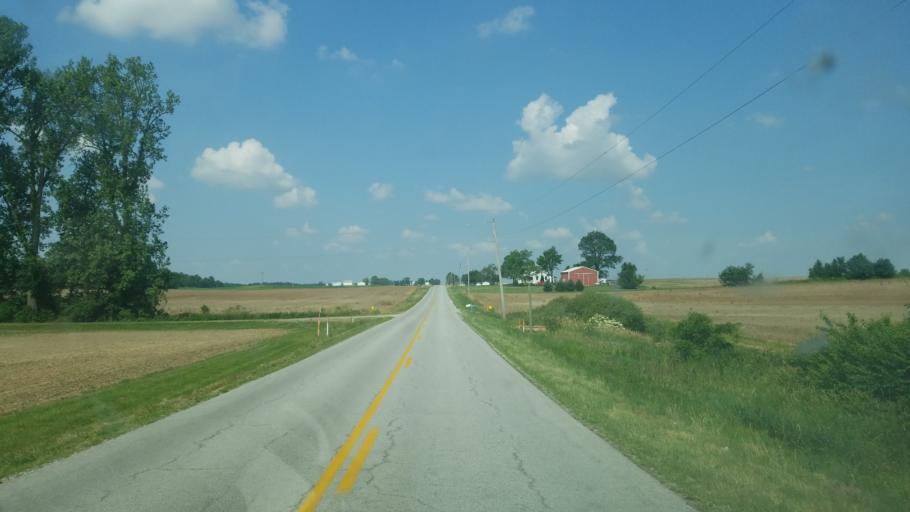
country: US
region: Ohio
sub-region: Auglaize County
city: Wapakoneta
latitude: 40.5708
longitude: -84.1007
